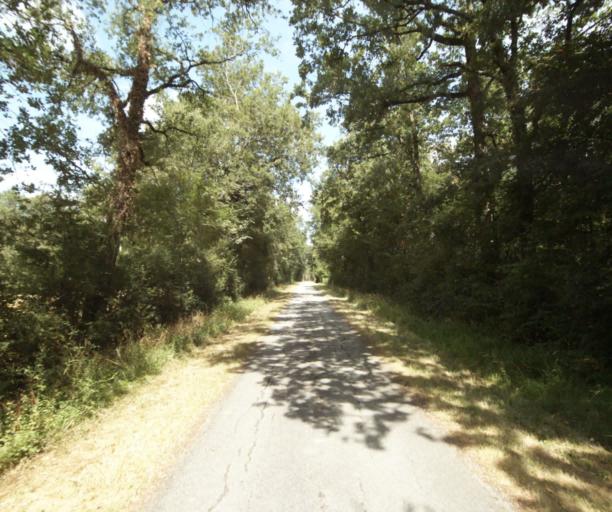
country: FR
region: Midi-Pyrenees
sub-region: Departement du Tarn
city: Dourgne
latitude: 43.4853
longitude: 2.1103
